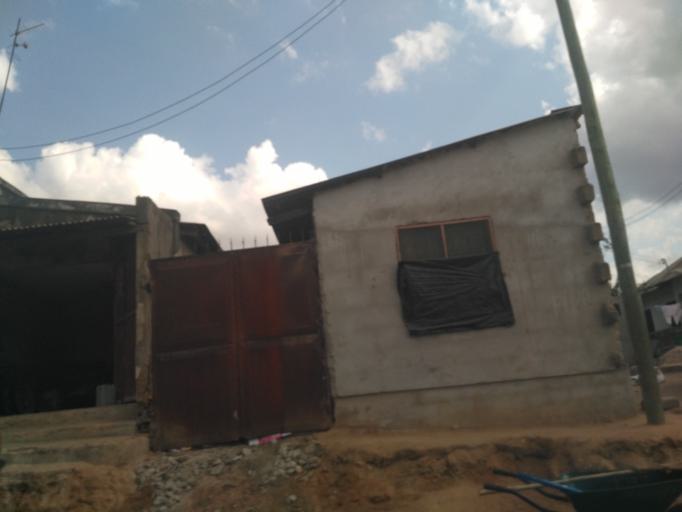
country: TZ
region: Dar es Salaam
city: Dar es Salaam
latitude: -6.8948
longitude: 39.2780
